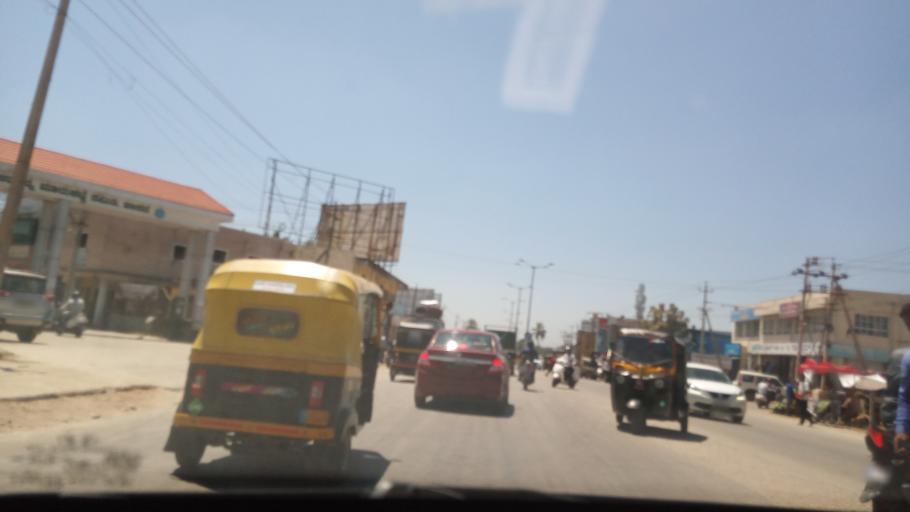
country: IN
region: Karnataka
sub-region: Hassan
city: Hassan
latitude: 12.9966
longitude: 76.0894
